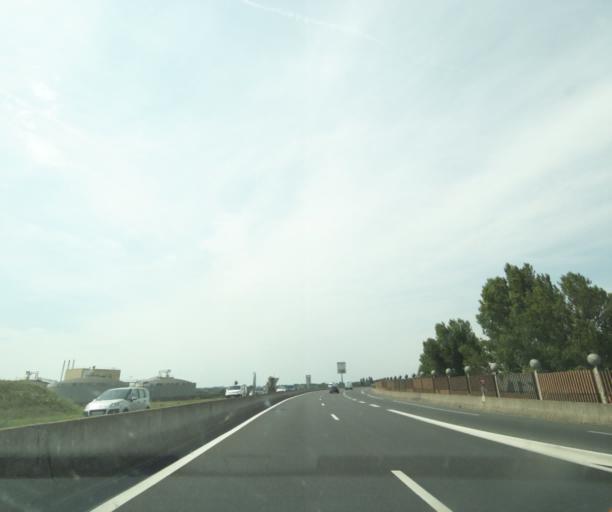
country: FR
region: Centre
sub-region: Departement d'Indre-et-Loire
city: La Riche
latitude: 47.3770
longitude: 0.6506
